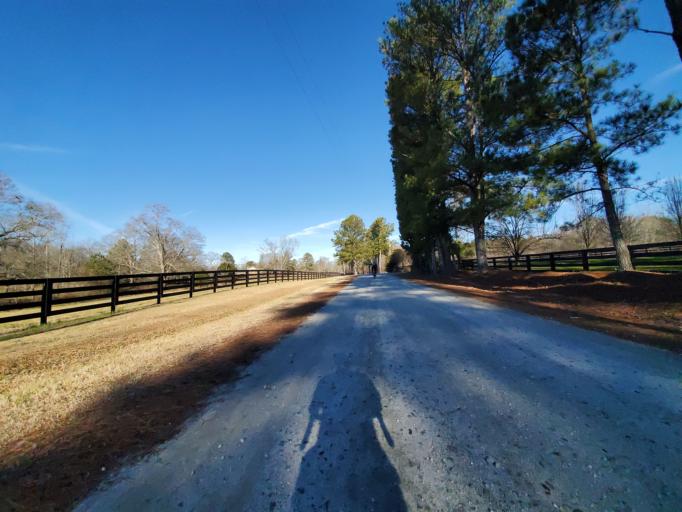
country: US
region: Georgia
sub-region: Fulton County
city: Chattahoochee Hills
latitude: 33.5491
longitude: -84.7939
